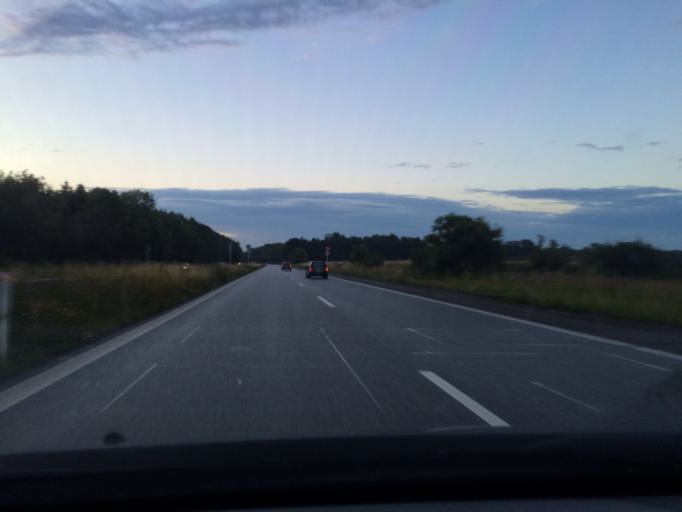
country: DK
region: Zealand
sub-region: Koge Kommune
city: Ejby
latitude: 55.4441
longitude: 12.1216
